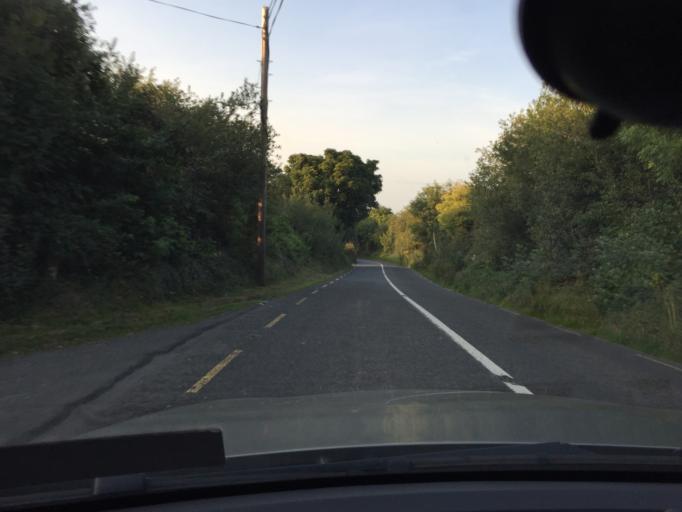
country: IE
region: Leinster
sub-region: Wicklow
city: Enniskerry
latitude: 53.1615
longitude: -6.1660
